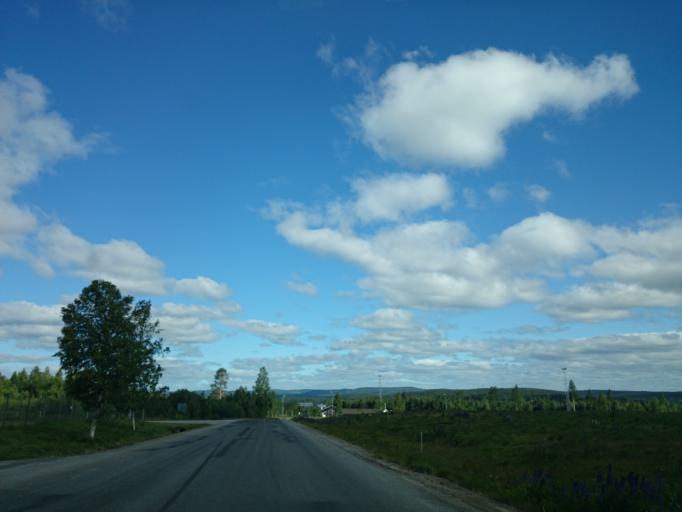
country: SE
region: Vaesternorrland
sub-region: Haernoesands Kommun
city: Haernoesand
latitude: 62.6534
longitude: 17.8903
